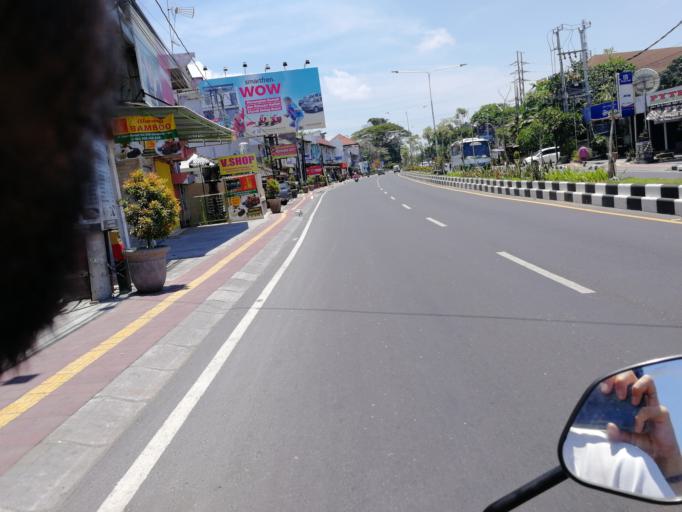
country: ID
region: Bali
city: Karyadharma
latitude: -8.6918
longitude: 115.1890
